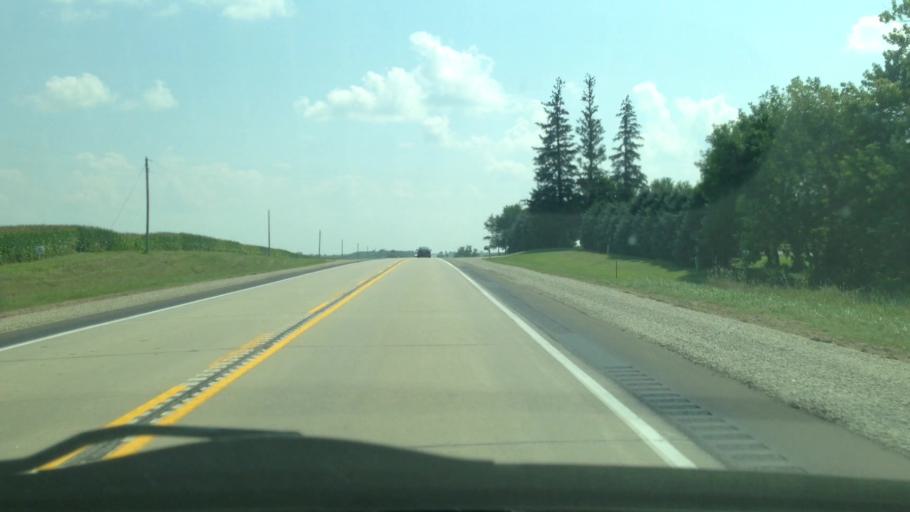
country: US
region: Iowa
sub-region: Howard County
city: Cresco
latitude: 43.4071
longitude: -92.2986
